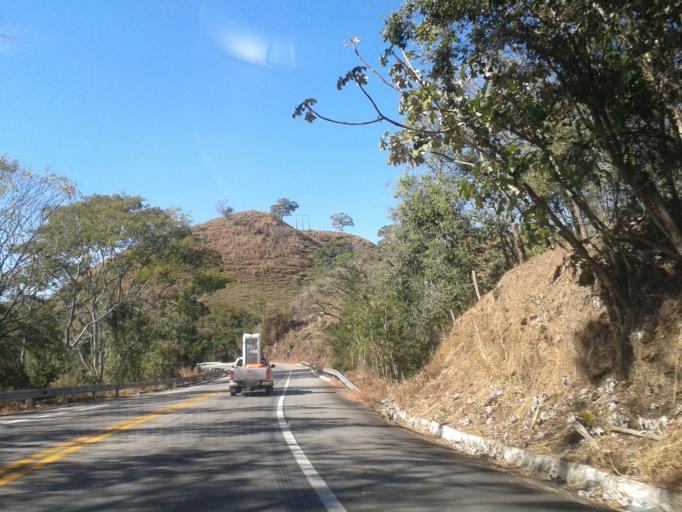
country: BR
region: Goias
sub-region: Goias
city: Goias
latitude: -15.9200
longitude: -50.1293
